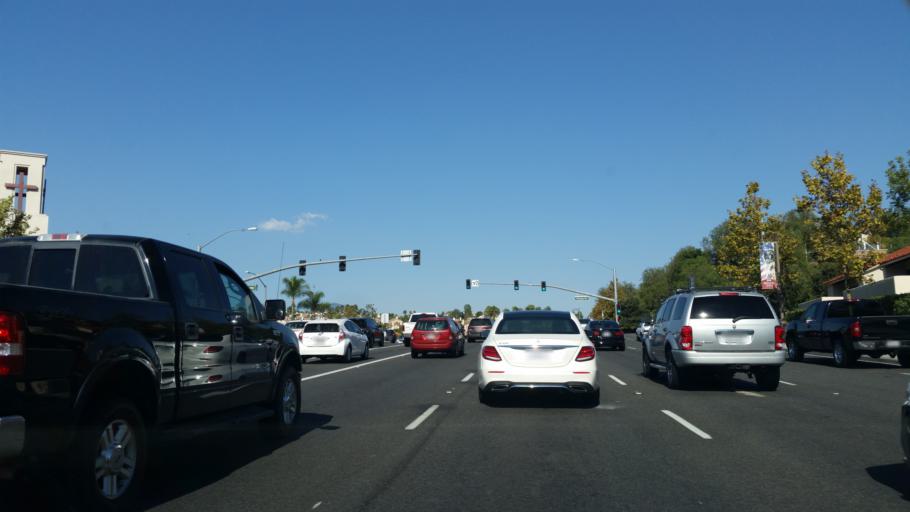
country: US
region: California
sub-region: Orange County
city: Mission Viejo
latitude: 33.5836
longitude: -117.6602
